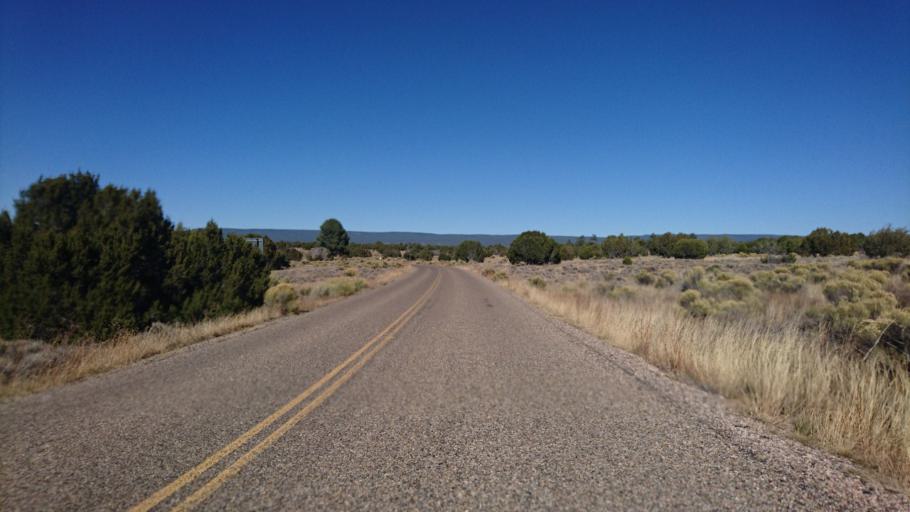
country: US
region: New Mexico
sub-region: McKinley County
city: Thoreau
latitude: 35.0398
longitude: -108.3391
